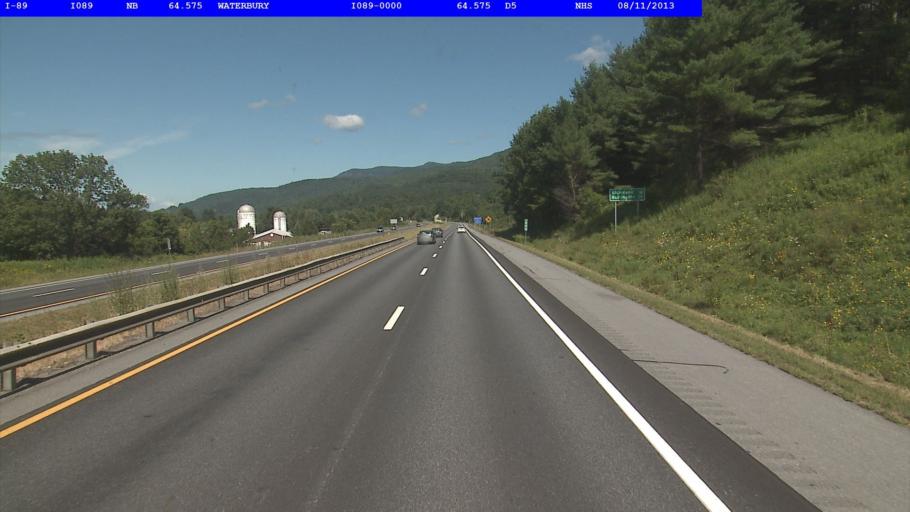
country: US
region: Vermont
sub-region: Washington County
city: Waterbury
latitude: 44.3467
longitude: -72.7673
